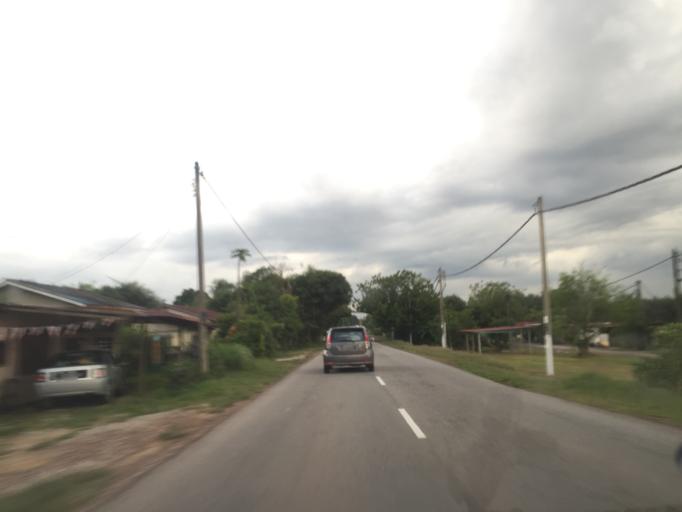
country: MY
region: Kedah
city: Sungai Petani
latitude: 5.5757
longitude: 100.4996
